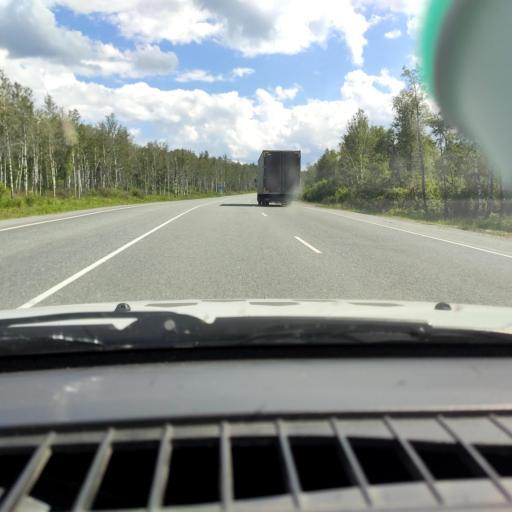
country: RU
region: Chelyabinsk
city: Zlatoust
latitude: 55.0480
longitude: 59.7230
